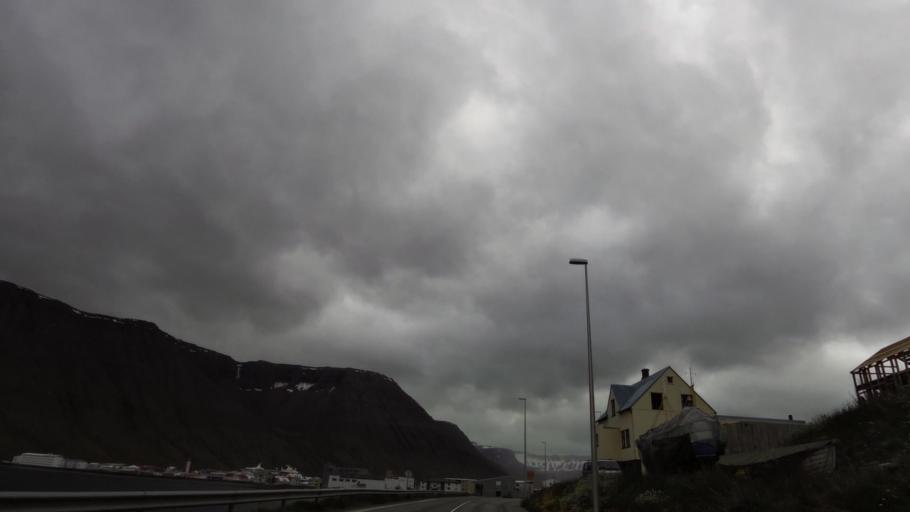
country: IS
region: Westfjords
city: Isafjoerdur
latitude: 66.0808
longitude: -23.1239
